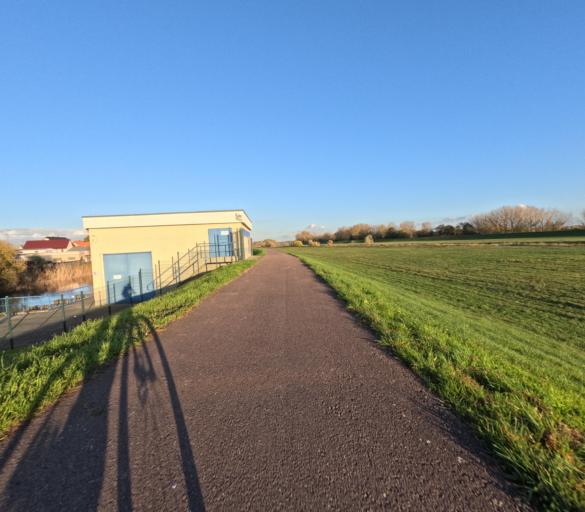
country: DE
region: Saxony-Anhalt
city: Rassnitz
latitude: 51.3897
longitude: 12.0955
